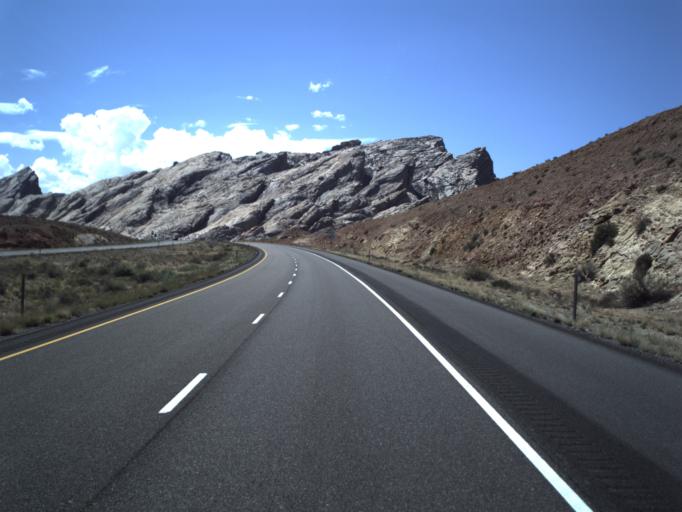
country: US
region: Utah
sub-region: Carbon County
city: East Carbon City
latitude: 38.9246
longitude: -110.4200
